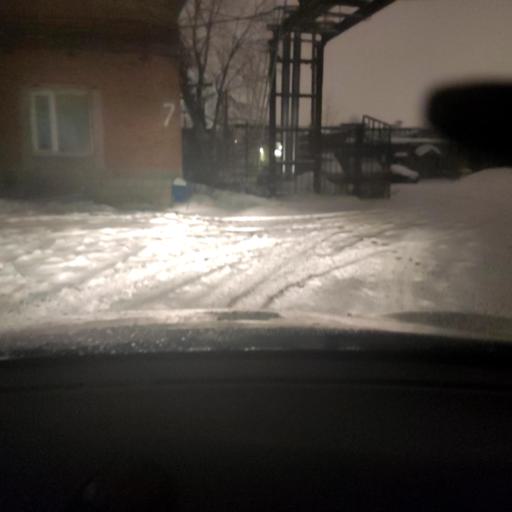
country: RU
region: Tatarstan
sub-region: Gorod Kazan'
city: Kazan
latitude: 55.8364
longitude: 49.0533
